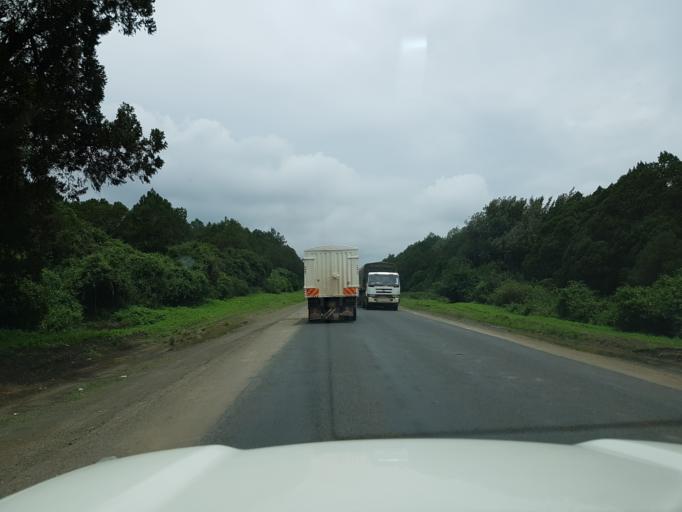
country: KE
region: Kiambu
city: Limuru
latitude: -1.0877
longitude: 36.6050
